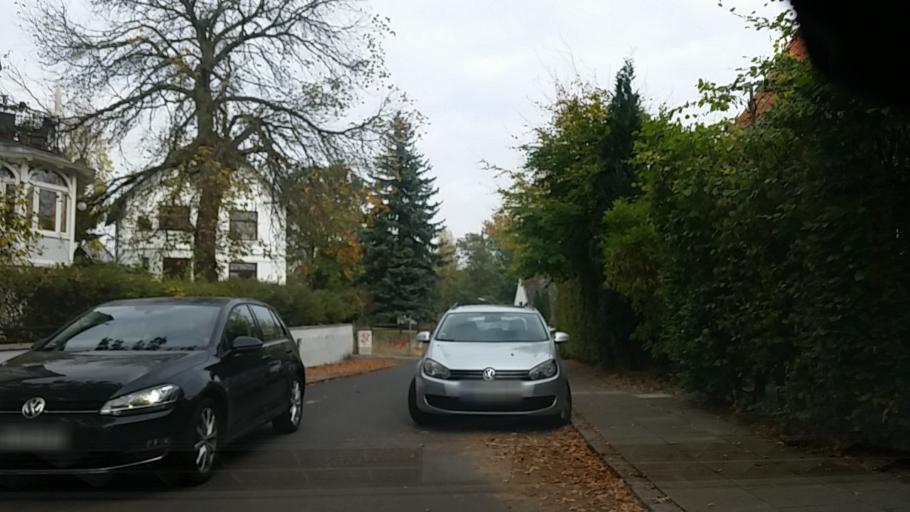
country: DE
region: Hamburg
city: Eidelstedt
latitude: 53.5579
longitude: 9.8700
